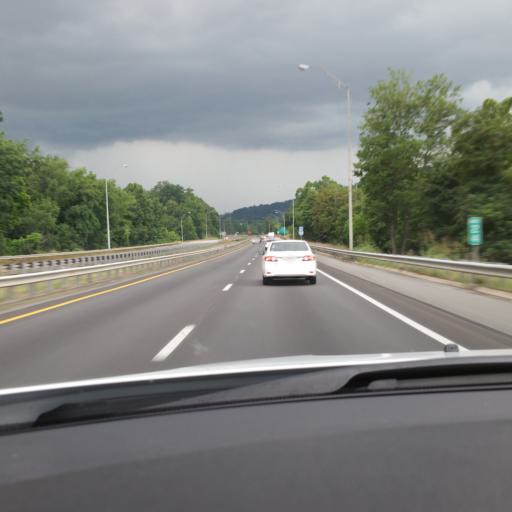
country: US
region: North Carolina
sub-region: Buncombe County
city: Woodfin
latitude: 35.6364
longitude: -82.5805
